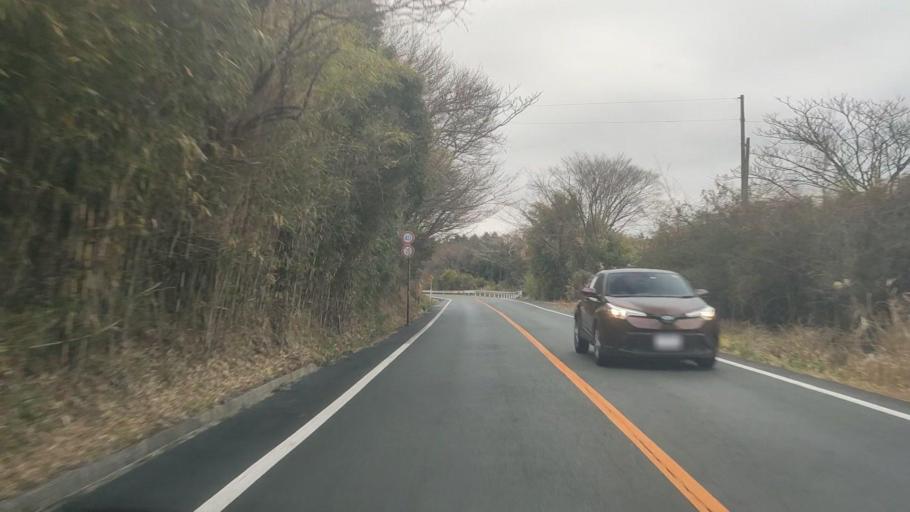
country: JP
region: Kumamoto
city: Aso
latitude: 32.8968
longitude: 131.0180
